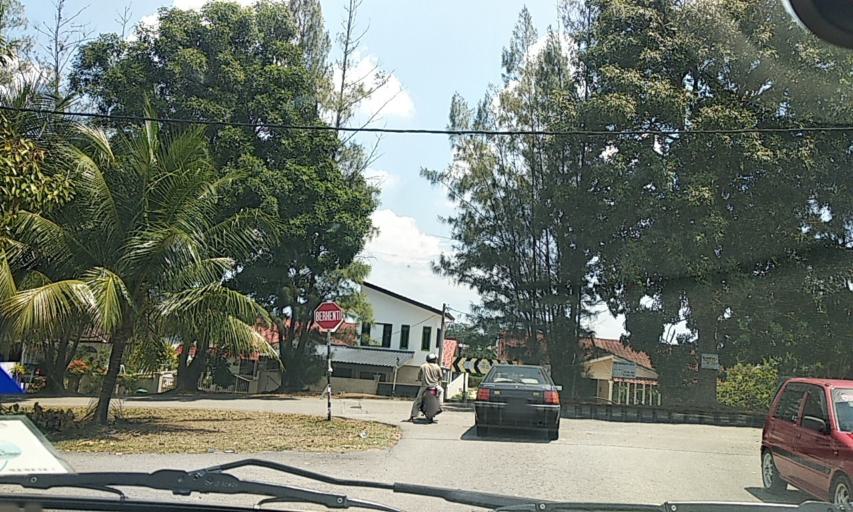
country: MY
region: Kedah
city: Sungai Petani
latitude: 5.6250
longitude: 100.4708
